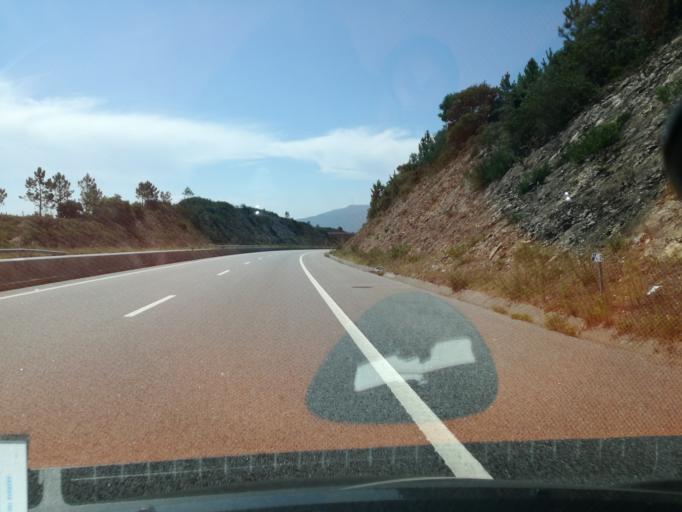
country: PT
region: Viana do Castelo
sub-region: Caminha
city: Vila Praia de Ancora
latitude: 41.8319
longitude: -8.7866
